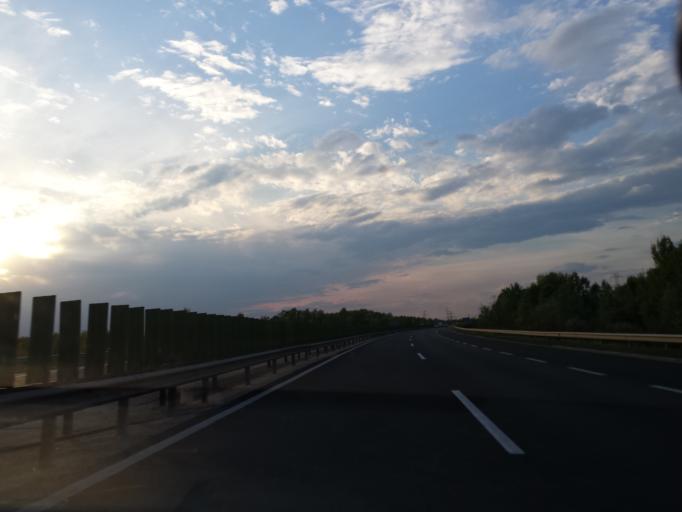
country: HU
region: Gyor-Moson-Sopron
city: Abda
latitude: 47.6797
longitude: 17.5443
